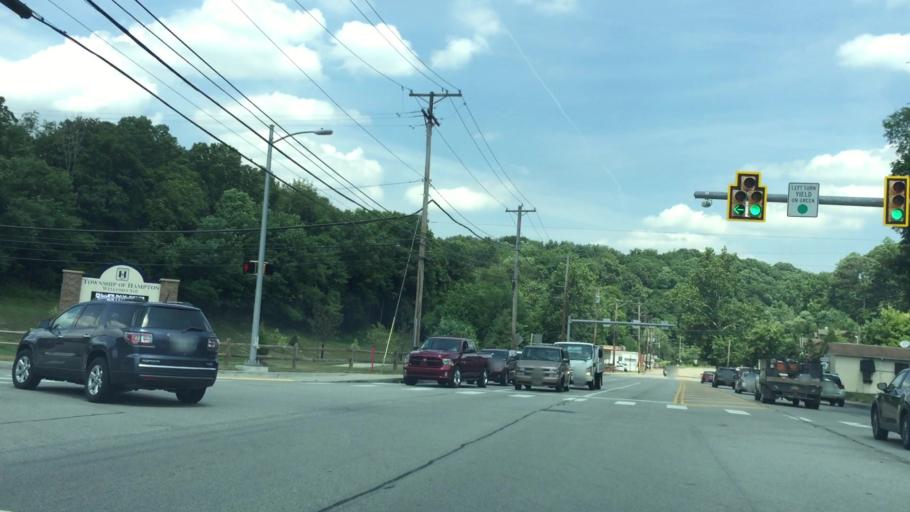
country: US
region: Pennsylvania
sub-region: Allegheny County
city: Allison Park
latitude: 40.5594
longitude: -79.9593
